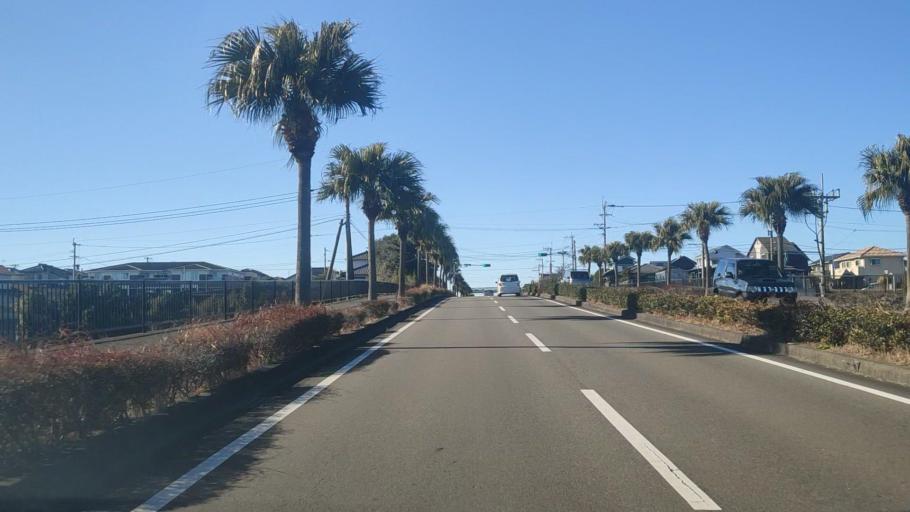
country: JP
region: Miyazaki
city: Miyazaki-shi
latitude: 31.9404
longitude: 131.4525
